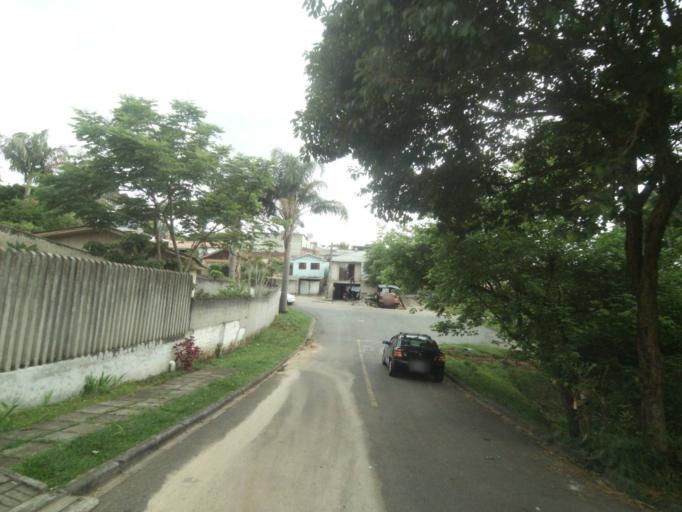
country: BR
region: Parana
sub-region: Curitiba
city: Curitiba
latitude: -25.3839
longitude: -49.2876
